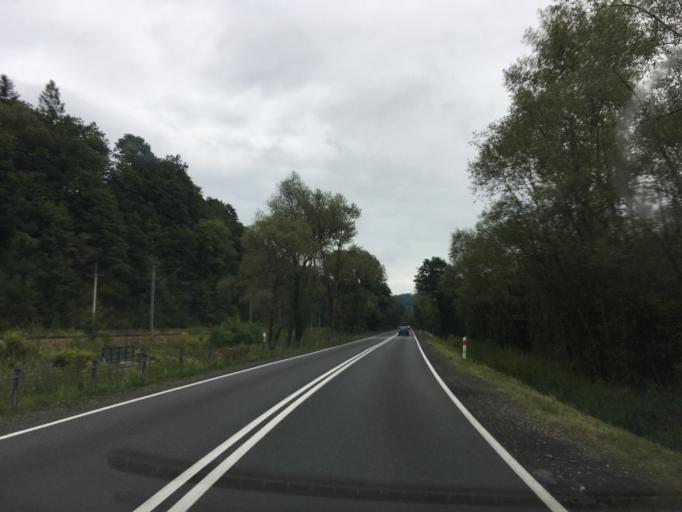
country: PL
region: Lesser Poland Voivodeship
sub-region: Powiat suski
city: Zembrzyce
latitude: 49.7685
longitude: 19.5923
